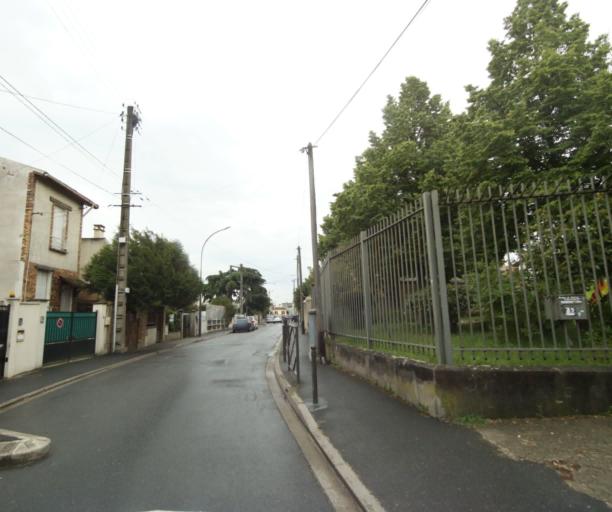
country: FR
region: Ile-de-France
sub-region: Departement du Val-d'Oise
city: Bezons
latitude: 48.9378
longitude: 2.2171
